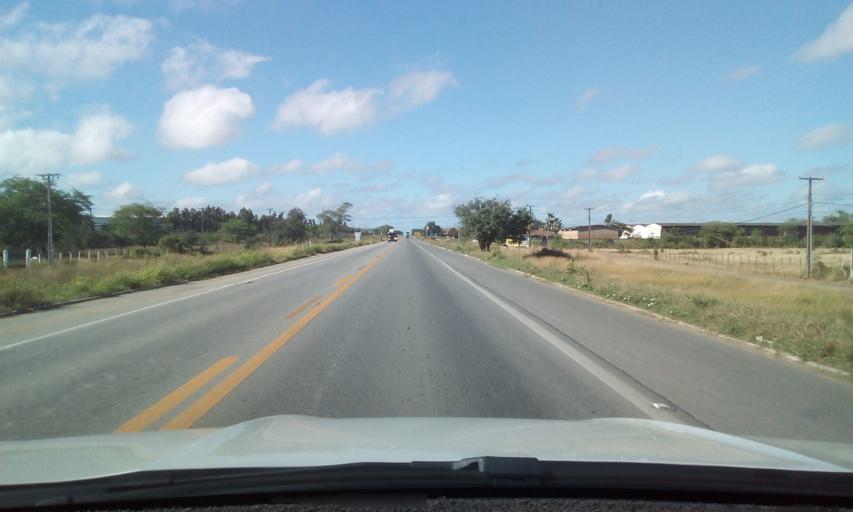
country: BR
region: Paraiba
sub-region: Campina Grande
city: Campina Grande
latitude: -7.2979
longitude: -35.8917
